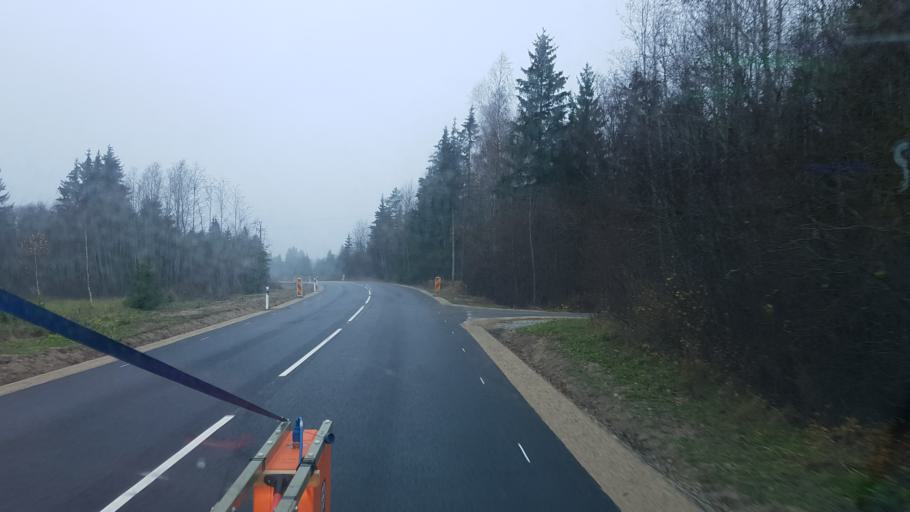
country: EE
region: Raplamaa
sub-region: Kohila vald
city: Kohila
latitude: 59.1759
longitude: 24.8342
